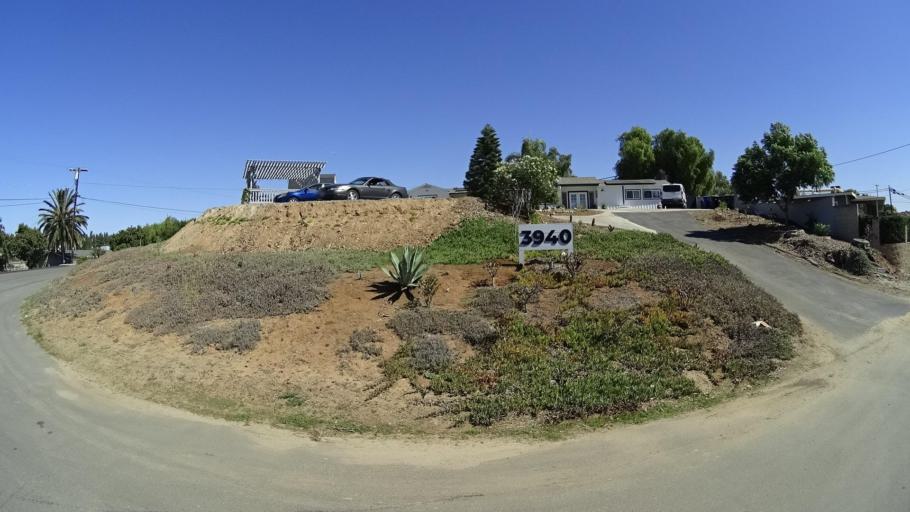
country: US
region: California
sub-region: San Diego County
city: Bonita
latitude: 32.6673
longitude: -117.0460
